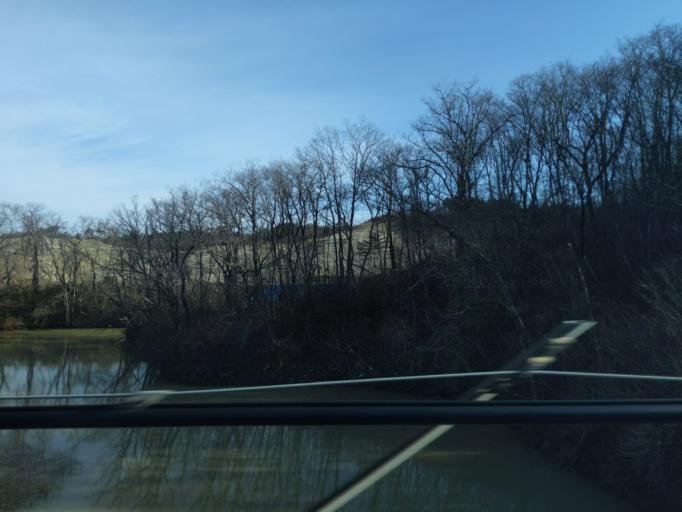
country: JP
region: Miyagi
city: Rifu
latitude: 38.4068
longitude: 140.9643
